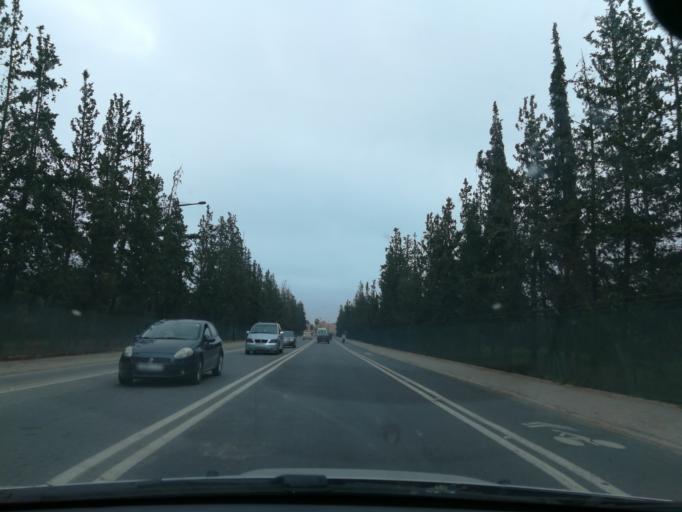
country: MA
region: Marrakech-Tensift-Al Haouz
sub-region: Marrakech
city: Marrakesh
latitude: 31.6031
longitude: -7.9758
